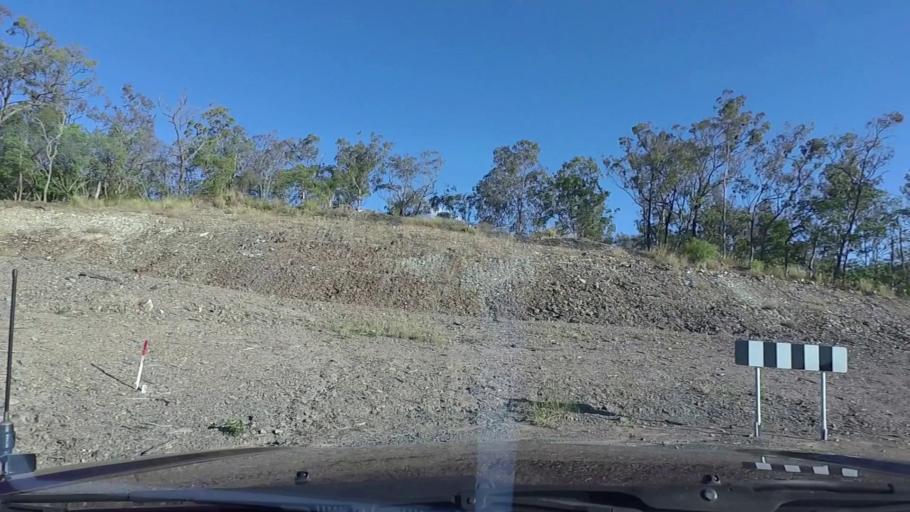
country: AU
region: Queensland
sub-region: Logan
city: Windaroo
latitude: -27.7246
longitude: 153.1696
